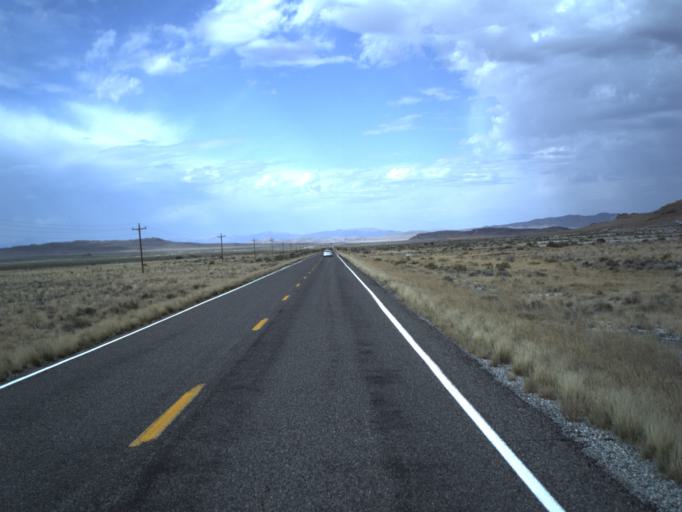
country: US
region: Utah
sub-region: Tooele County
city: Wendover
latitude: 41.4292
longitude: -113.8158
